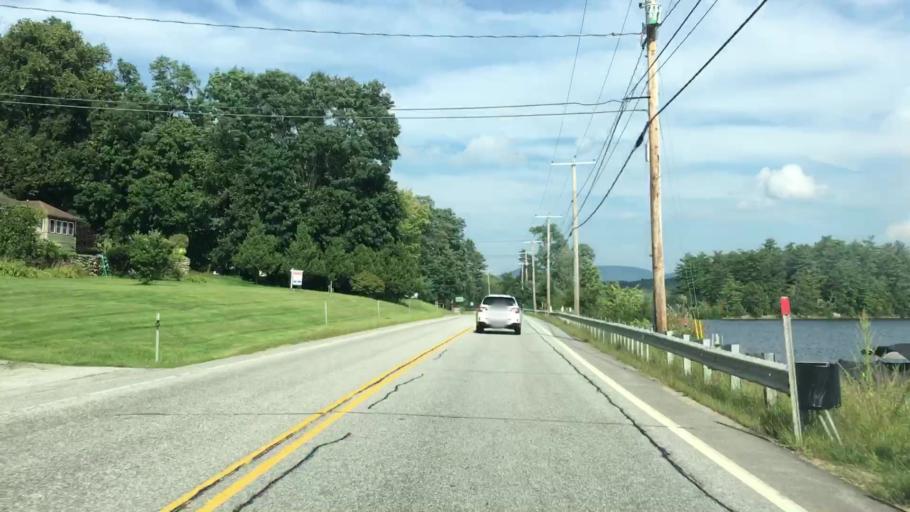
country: US
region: New Hampshire
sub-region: Belknap County
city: Sanbornton
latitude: 43.4933
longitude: -71.5242
